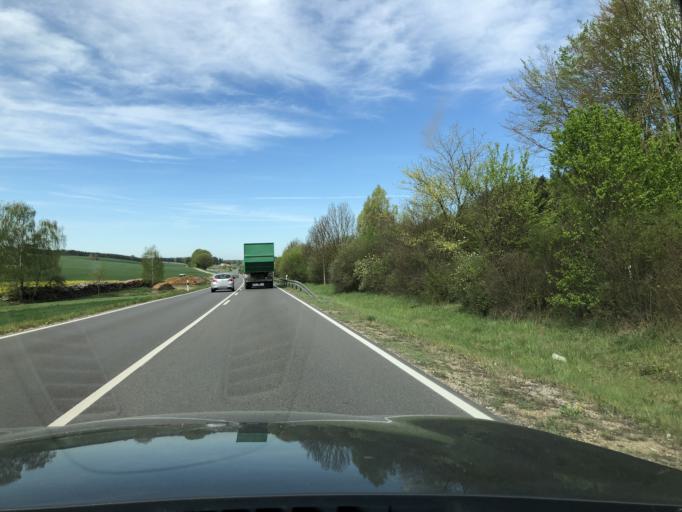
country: DE
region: Bavaria
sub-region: Swabia
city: Laugna
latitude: 48.5371
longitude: 10.7420
